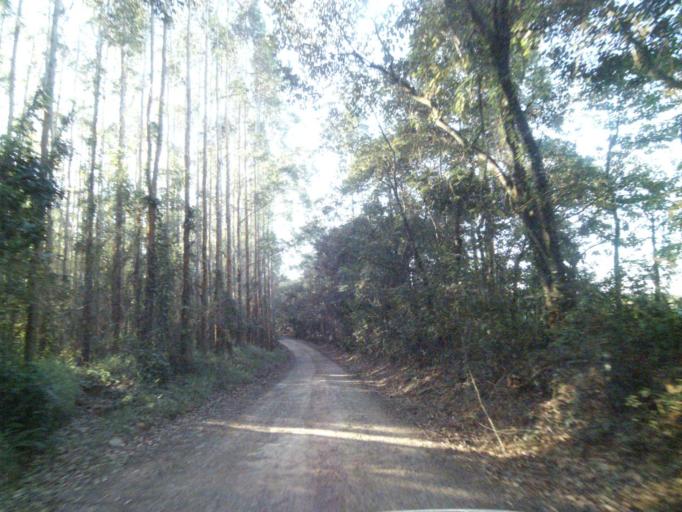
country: BR
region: Parana
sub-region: Telemaco Borba
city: Telemaco Borba
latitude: -24.5016
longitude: -50.5980
